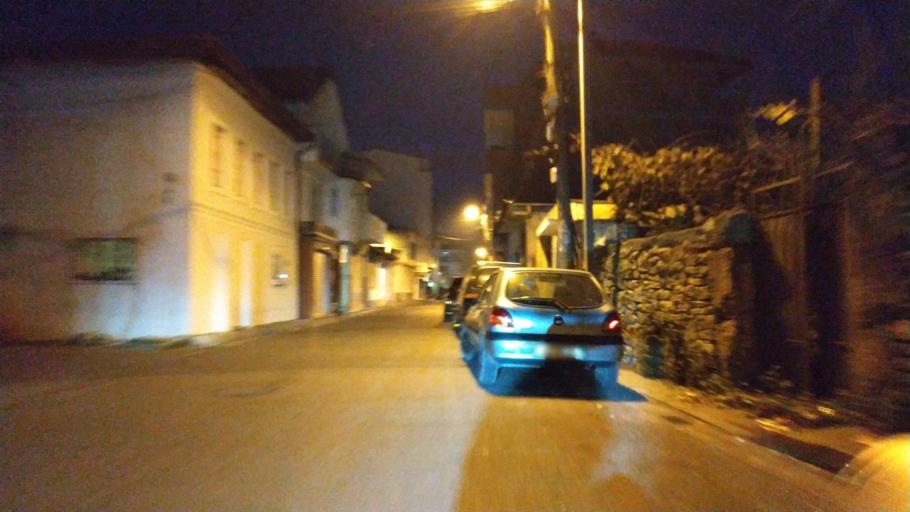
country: AL
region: Shkoder
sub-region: Rrethi i Shkodres
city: Shkoder
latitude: 42.0660
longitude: 19.5068
